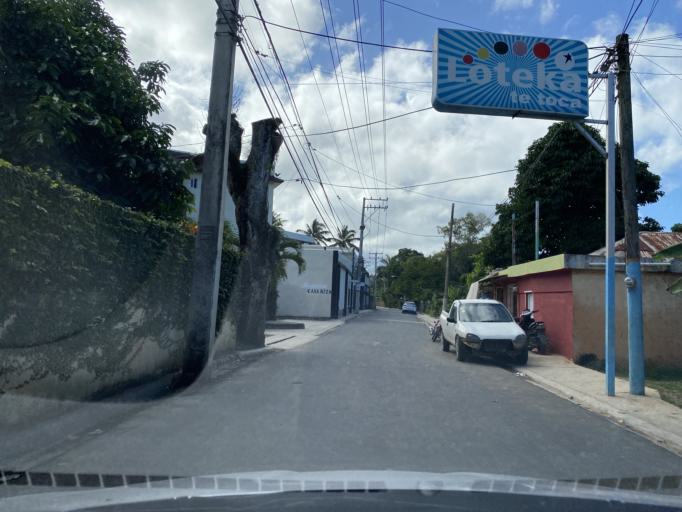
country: DO
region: Samana
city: Las Terrenas
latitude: 19.3096
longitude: -69.5505
